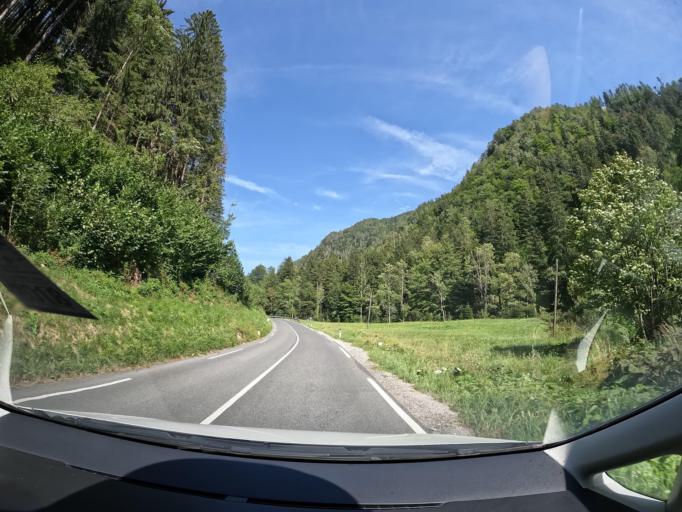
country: SI
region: Zirovnica
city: Zirovnica
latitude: 46.4421
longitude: 14.1818
